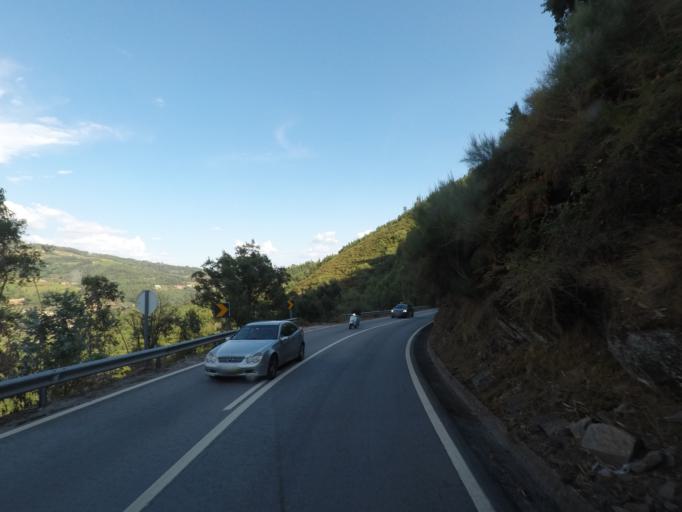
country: PT
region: Vila Real
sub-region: Mesao Frio
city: Mesao Frio
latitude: 41.1750
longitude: -7.9158
